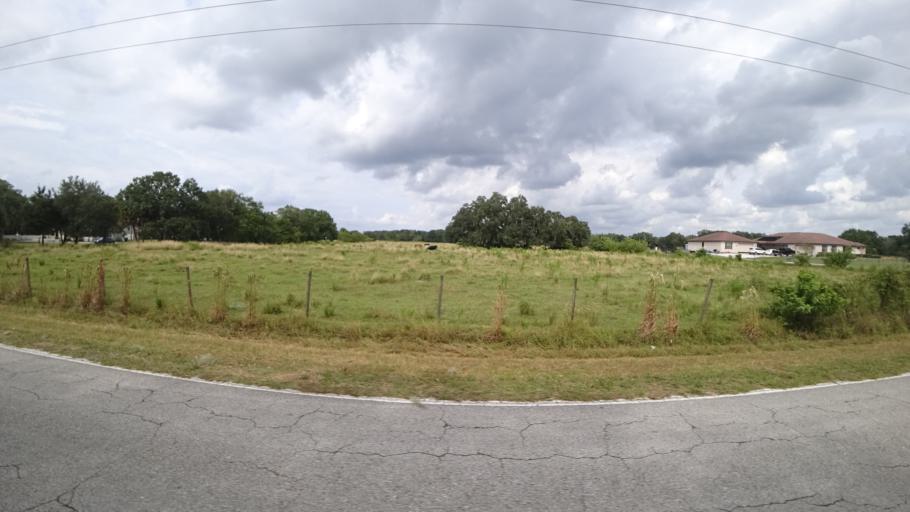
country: US
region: Florida
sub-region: Manatee County
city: Ellenton
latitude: 27.4878
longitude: -82.3799
